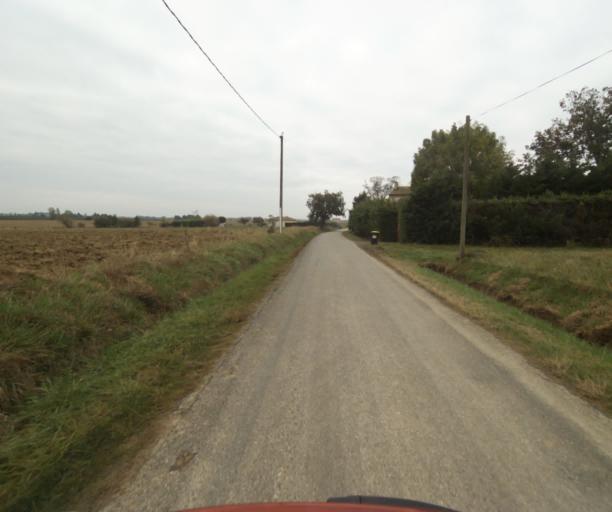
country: FR
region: Midi-Pyrenees
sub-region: Departement du Tarn-et-Garonne
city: Verdun-sur-Garonne
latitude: 43.8179
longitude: 1.2010
